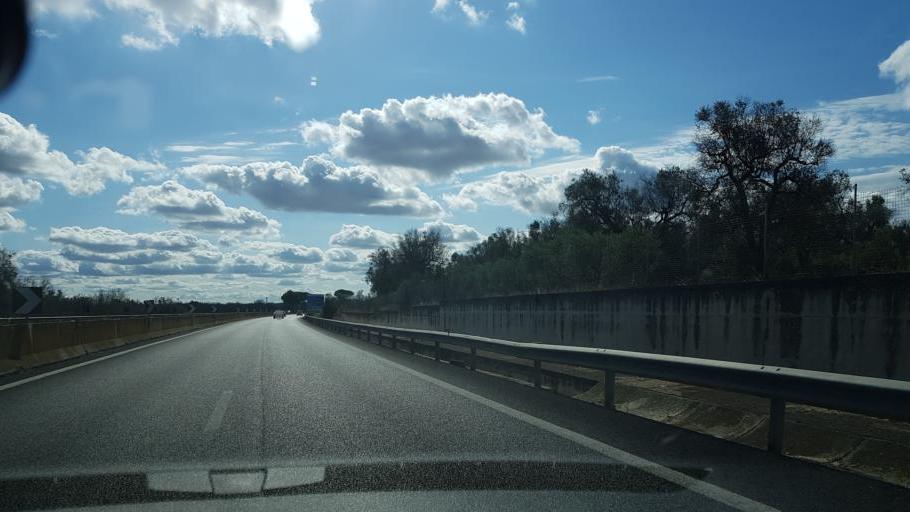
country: IT
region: Apulia
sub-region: Provincia di Lecce
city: Squinzano
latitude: 40.4459
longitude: 18.0730
